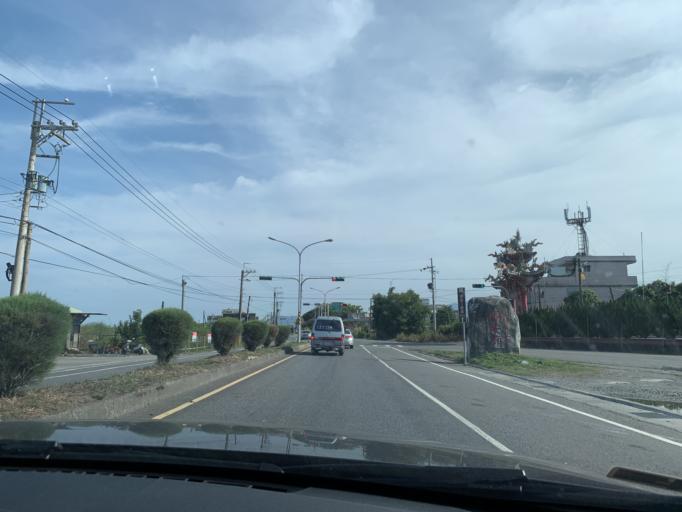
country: TW
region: Taiwan
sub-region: Yilan
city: Yilan
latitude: 24.7341
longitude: 121.8184
